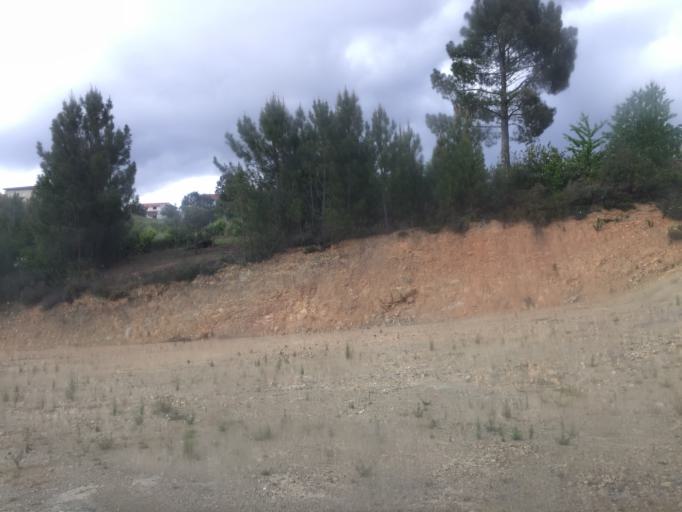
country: PT
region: Coimbra
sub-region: Pampilhosa da Serra
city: Pampilhosa da Serra
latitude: 40.0413
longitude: -8.0047
